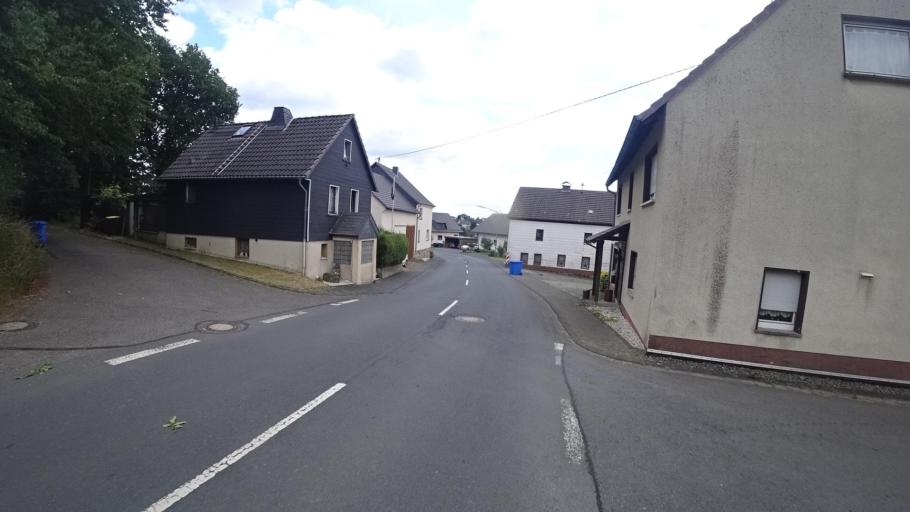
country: DE
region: Rheinland-Pfalz
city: Weyerbusch
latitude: 50.7164
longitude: 7.5410
